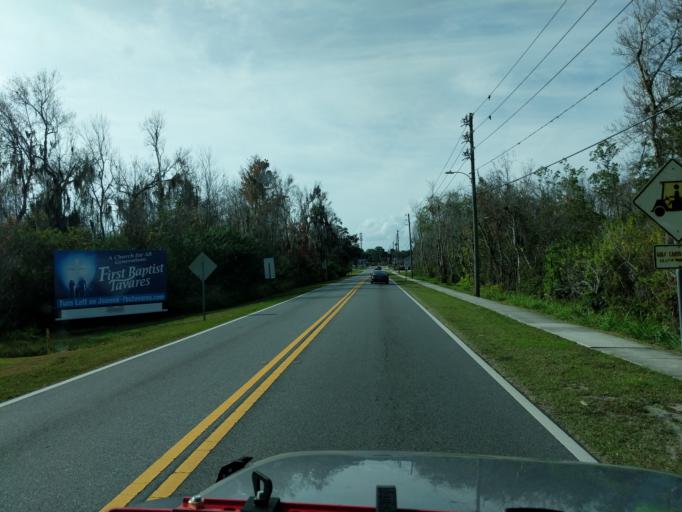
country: US
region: Florida
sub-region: Lake County
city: Tavares
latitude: 28.8041
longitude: -81.7206
